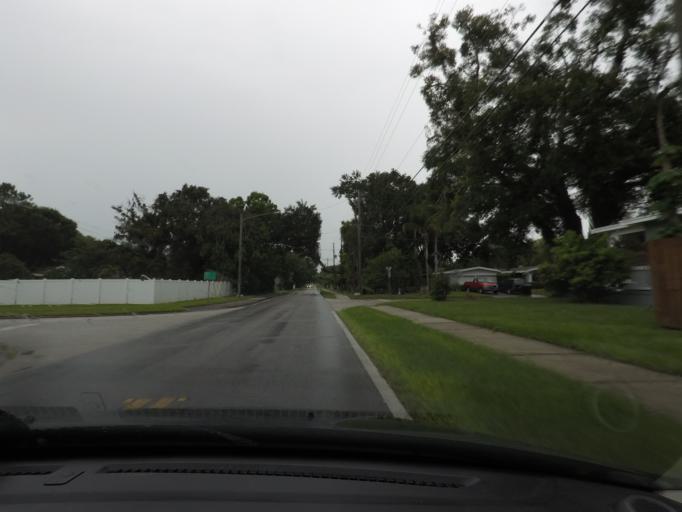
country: US
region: Florida
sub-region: Orange County
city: Edgewood
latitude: 28.4986
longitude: -81.3558
